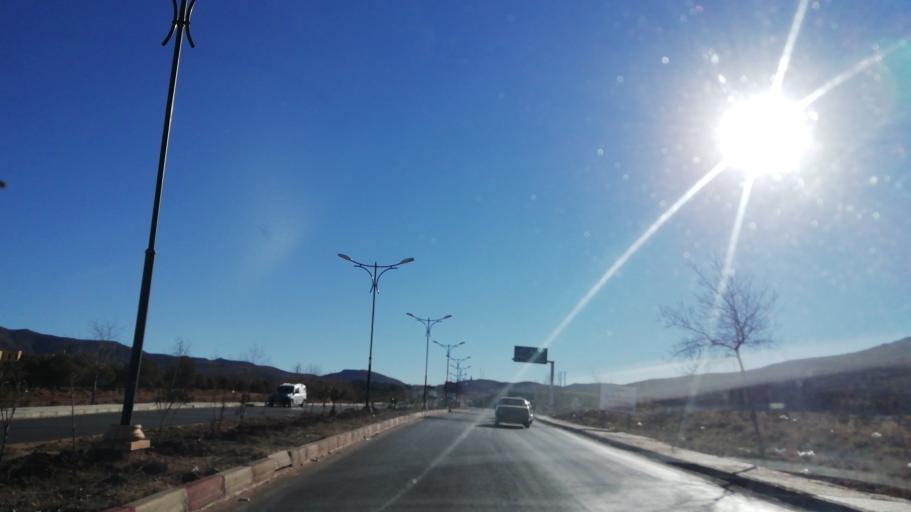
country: DZ
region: El Bayadh
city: El Bayadh
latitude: 33.6581
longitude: 1.0652
